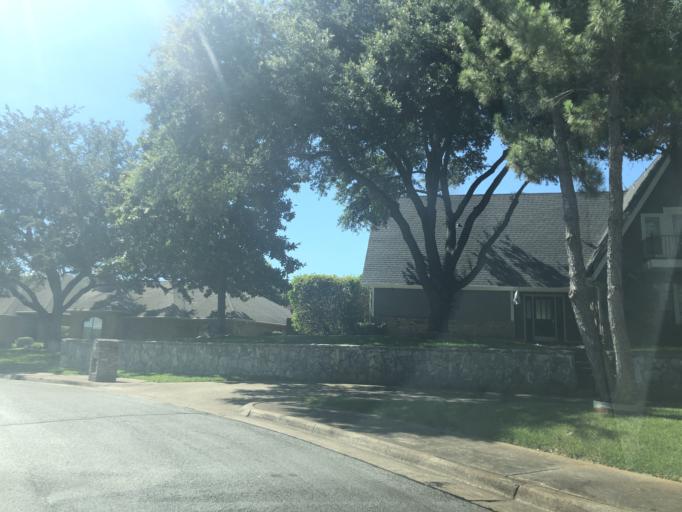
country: US
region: Texas
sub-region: Dallas County
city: Duncanville
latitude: 32.6346
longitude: -96.9294
